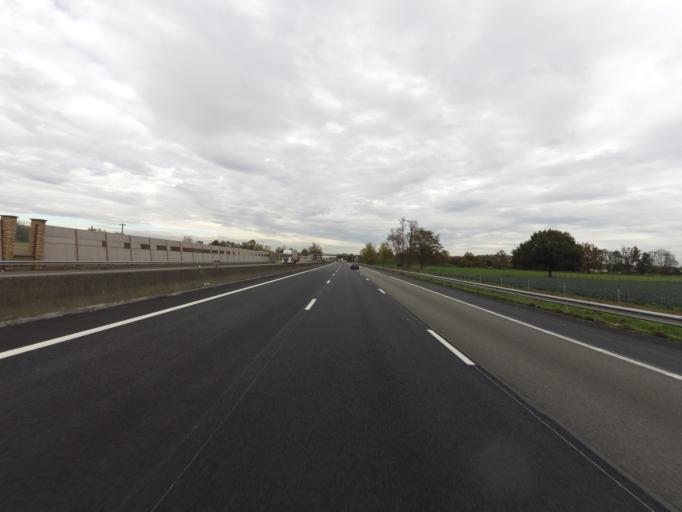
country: FR
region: Rhone-Alpes
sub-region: Departement du Rhone
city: Saint-Georges-de-Reneins
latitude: 46.0643
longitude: 4.7387
